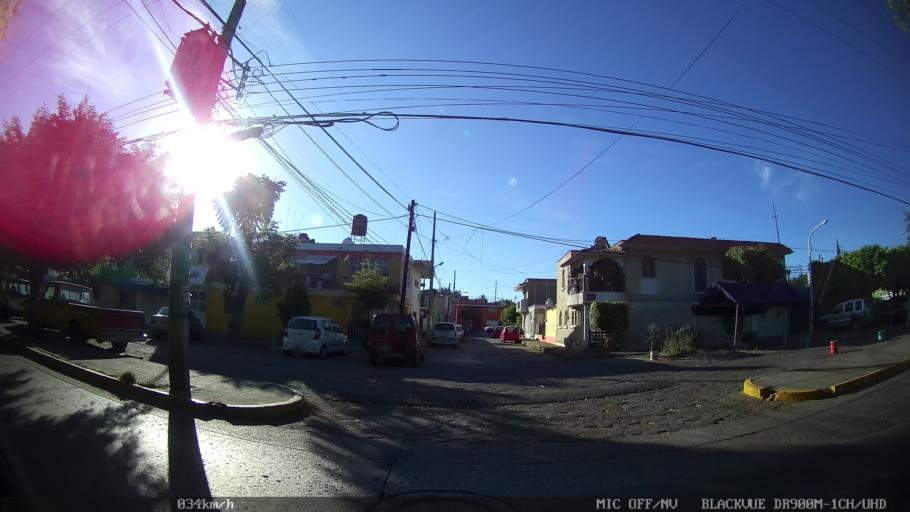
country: MX
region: Jalisco
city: Tlaquepaque
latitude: 20.6291
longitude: -103.3197
